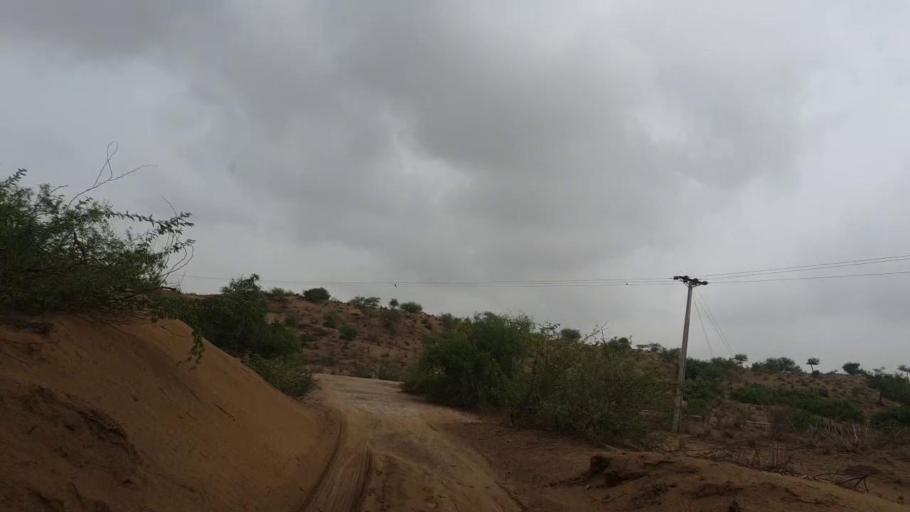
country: PK
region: Sindh
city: Diplo
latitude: 24.5121
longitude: 69.5012
